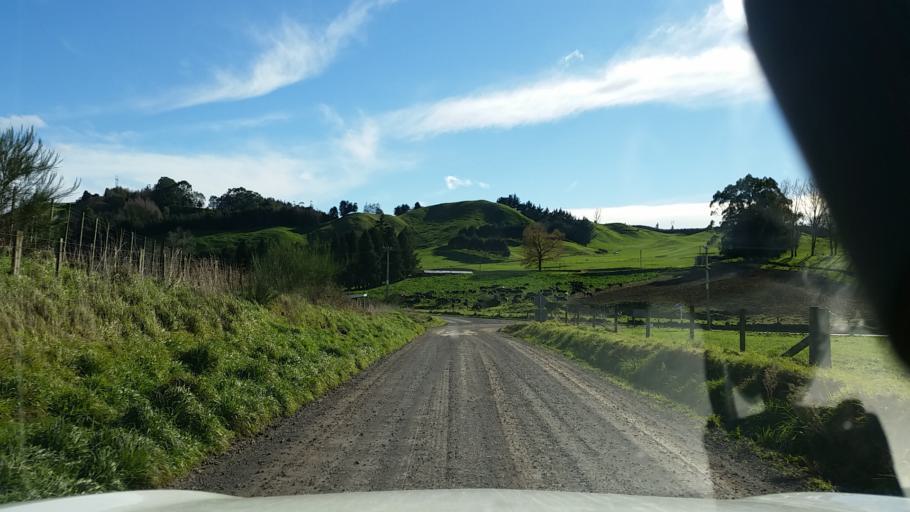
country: NZ
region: Bay of Plenty
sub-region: Rotorua District
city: Rotorua
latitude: -38.3536
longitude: 176.2317
